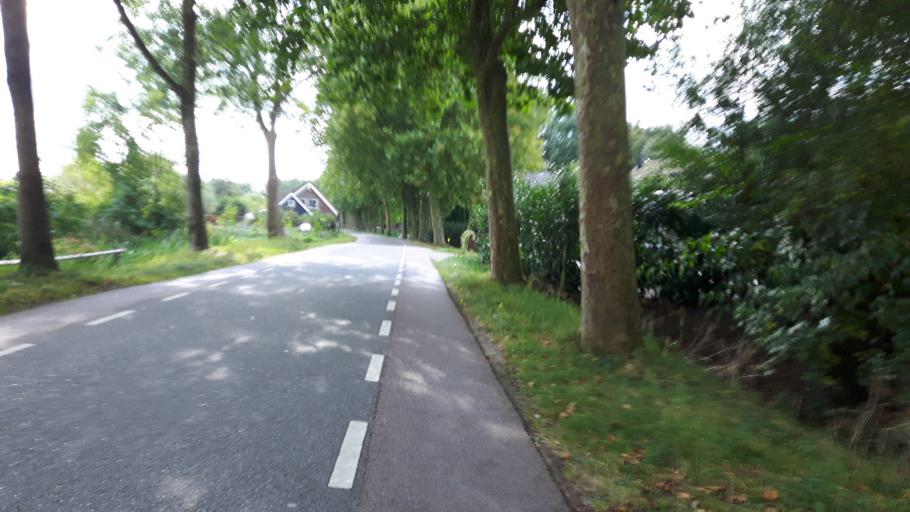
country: NL
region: Utrecht
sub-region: Gemeente Montfoort
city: Montfoort
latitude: 52.0914
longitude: 4.9520
